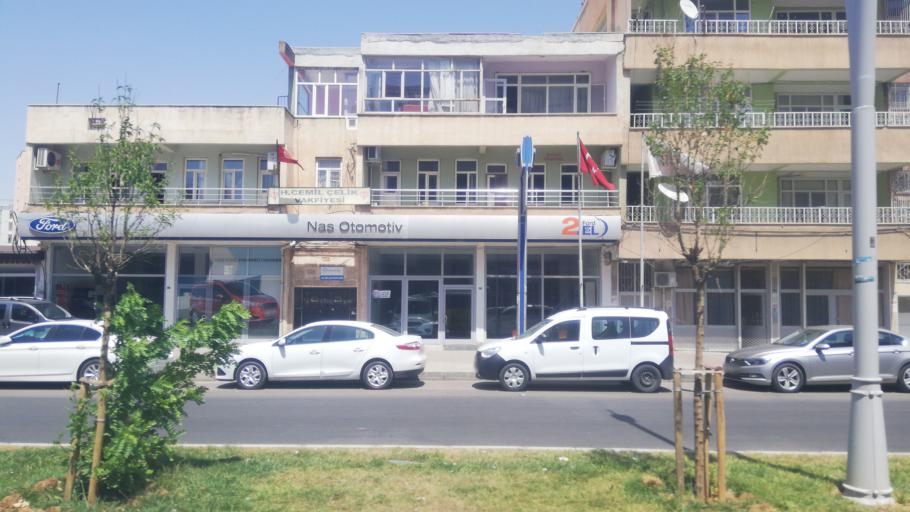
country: TR
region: Mardin
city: Midyat
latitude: 37.4228
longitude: 41.3458
